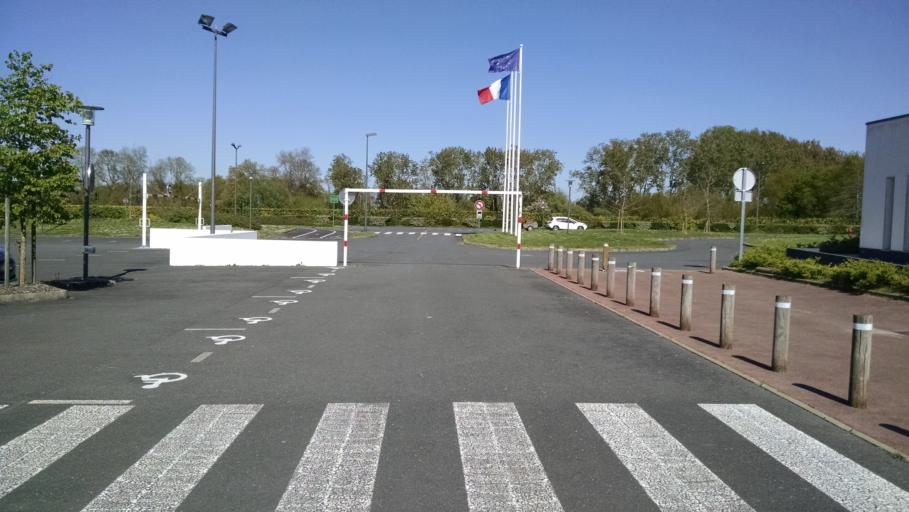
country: FR
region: Pays de la Loire
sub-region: Departement de la Loire-Atlantique
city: Haute-Goulaine
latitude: 47.1931
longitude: -1.4440
